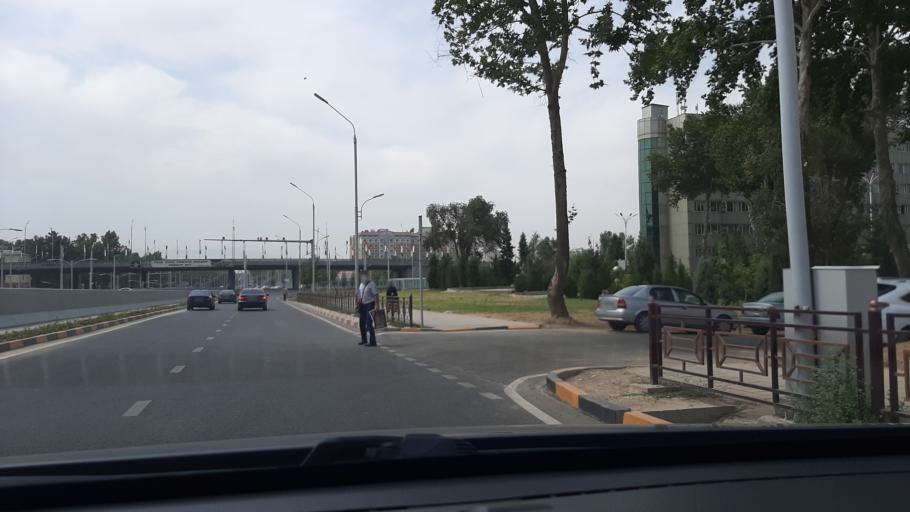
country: TJ
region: Dushanbe
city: Dushanbe
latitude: 38.5863
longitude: 68.7551
